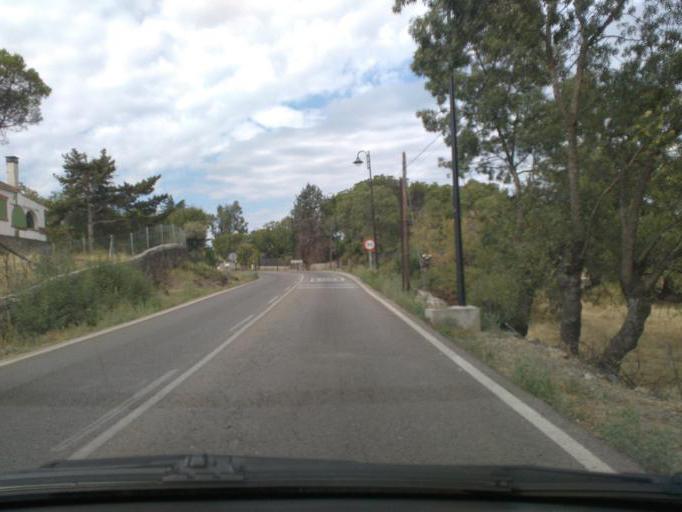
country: ES
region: Madrid
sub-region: Provincia de Madrid
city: Galapagar
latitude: 40.5772
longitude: -3.9933
